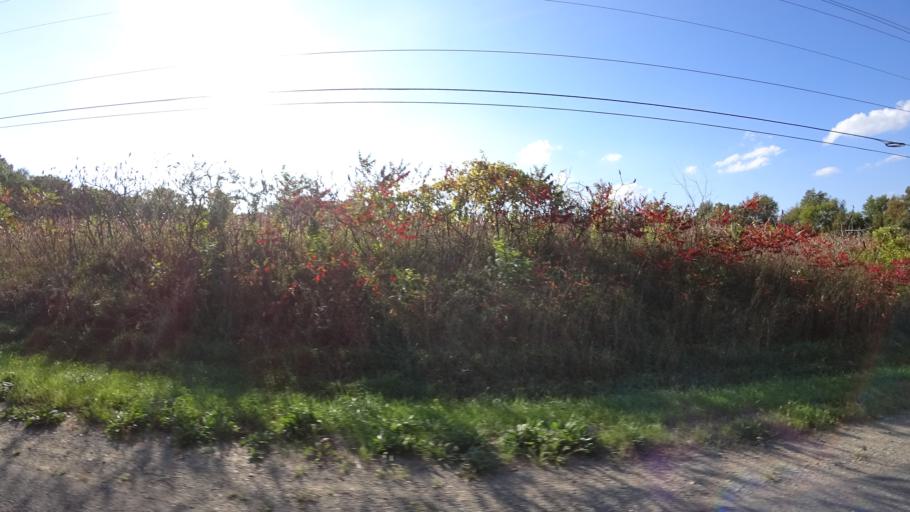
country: US
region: Michigan
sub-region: Saint Joseph County
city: Centreville
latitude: 41.8690
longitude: -85.5067
